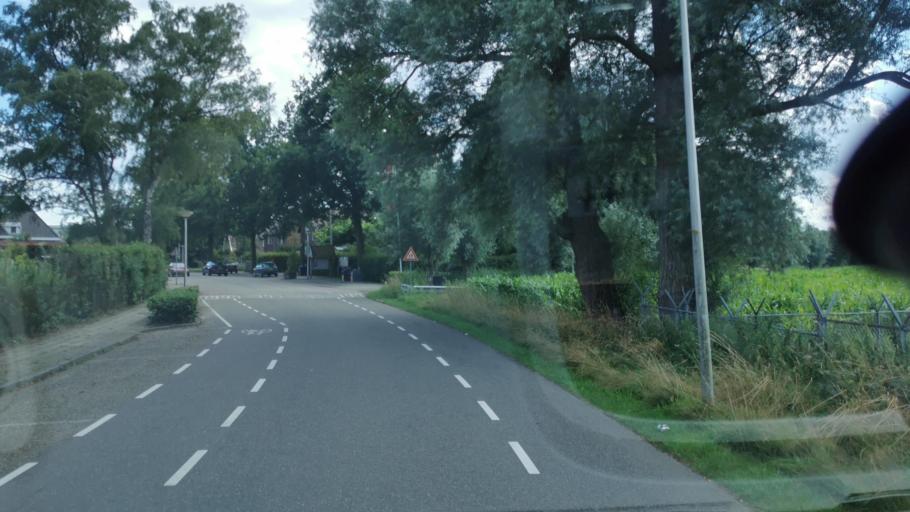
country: NL
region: Overijssel
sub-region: Gemeente Losser
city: Losser
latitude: 52.2330
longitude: 7.0032
